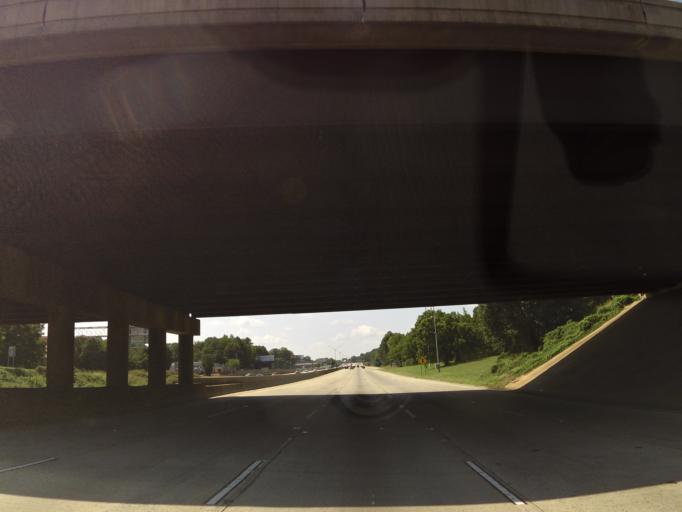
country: US
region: North Carolina
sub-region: Mecklenburg County
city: Charlotte
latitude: 35.2385
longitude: -80.9195
